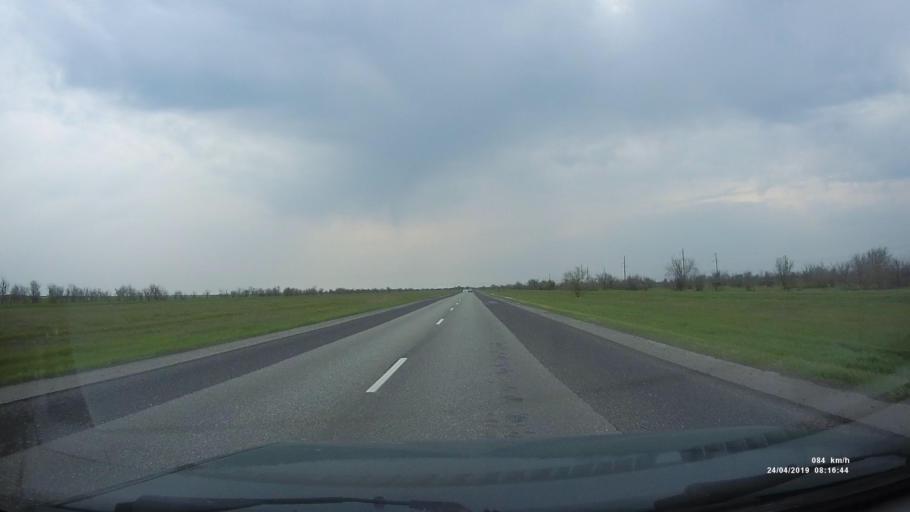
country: RU
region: Kalmykiya
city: Priyutnoye
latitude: 46.0986
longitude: 43.6175
